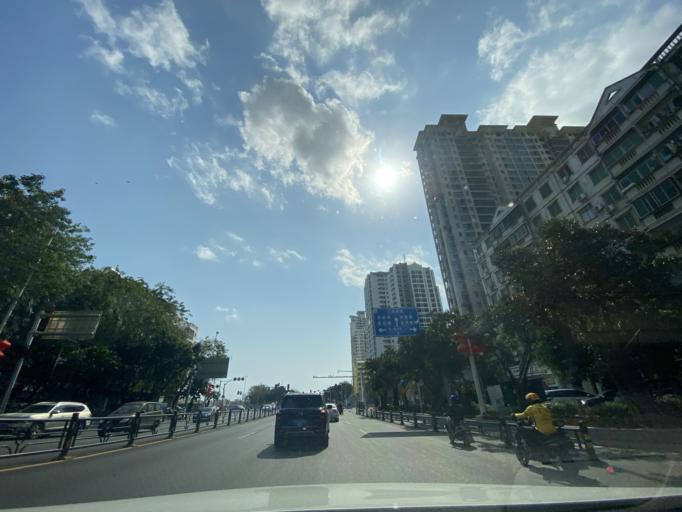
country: CN
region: Hainan
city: Sanya
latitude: 18.2645
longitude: 109.4941
